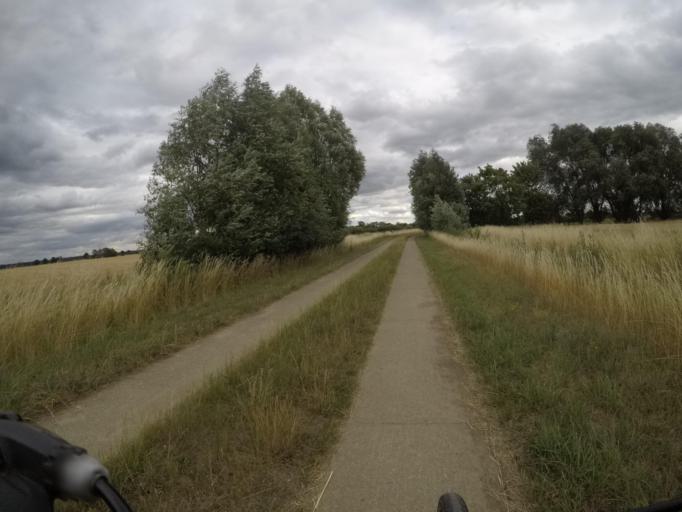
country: DE
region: Lower Saxony
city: Neu Darchau
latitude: 53.2414
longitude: 10.9294
